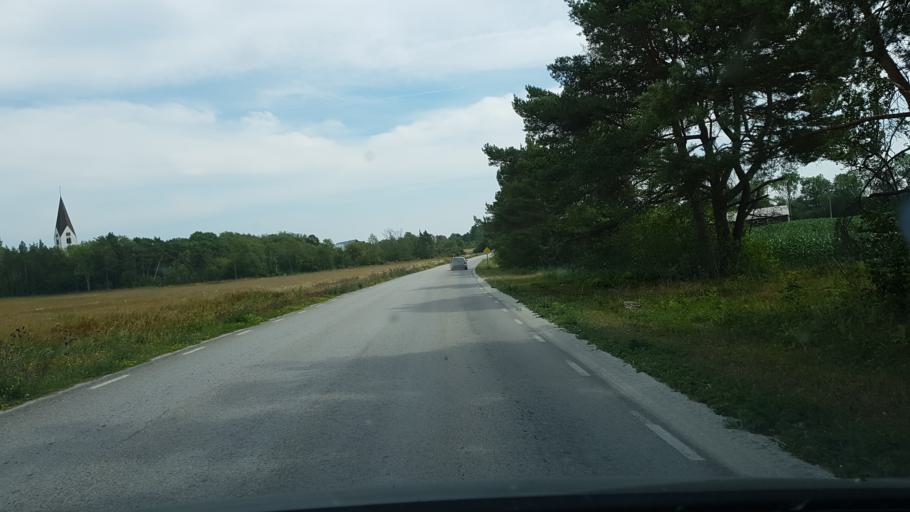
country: SE
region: Gotland
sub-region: Gotland
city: Slite
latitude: 57.7489
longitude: 18.7319
